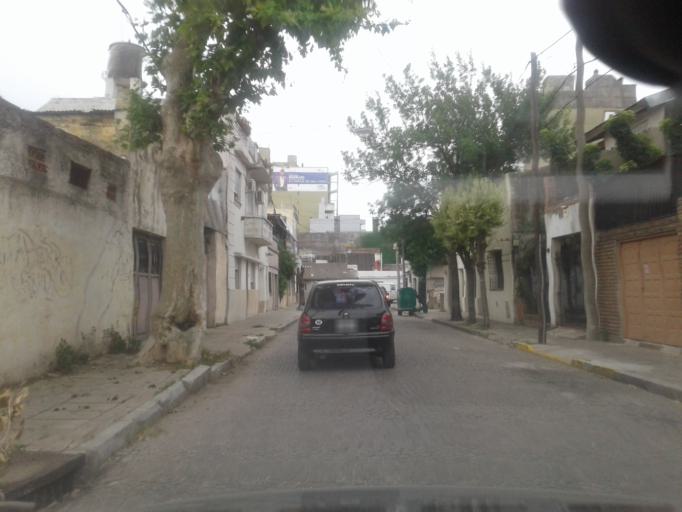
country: AR
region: Santa Fe
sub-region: Departamento de Rosario
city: Rosario
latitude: -32.9215
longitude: -60.6821
